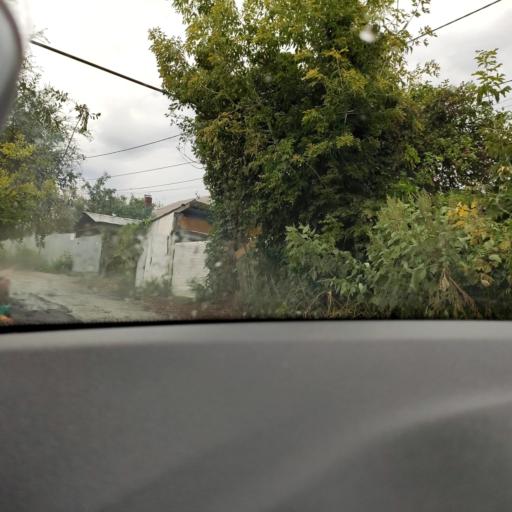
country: RU
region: Samara
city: Samara
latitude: 53.1737
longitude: 50.1576
